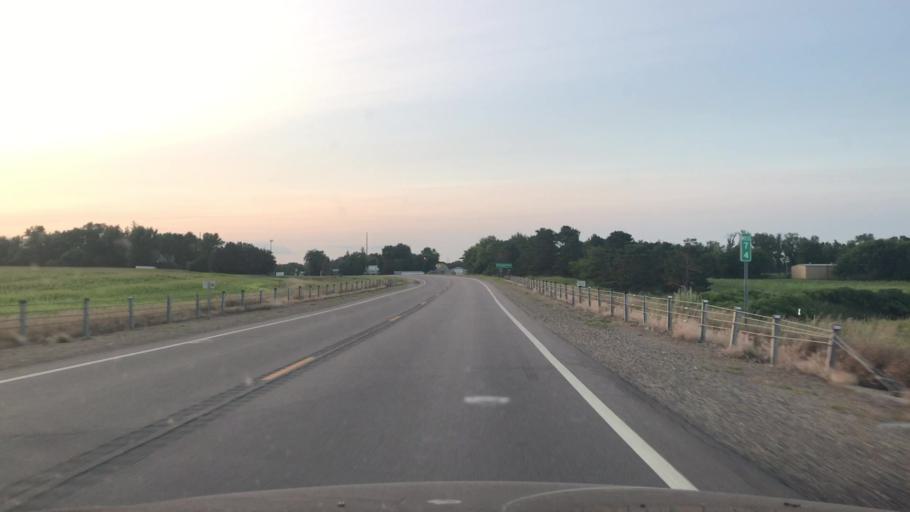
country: US
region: Minnesota
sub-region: Redwood County
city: Redwood Falls
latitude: 44.5217
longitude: -95.1180
